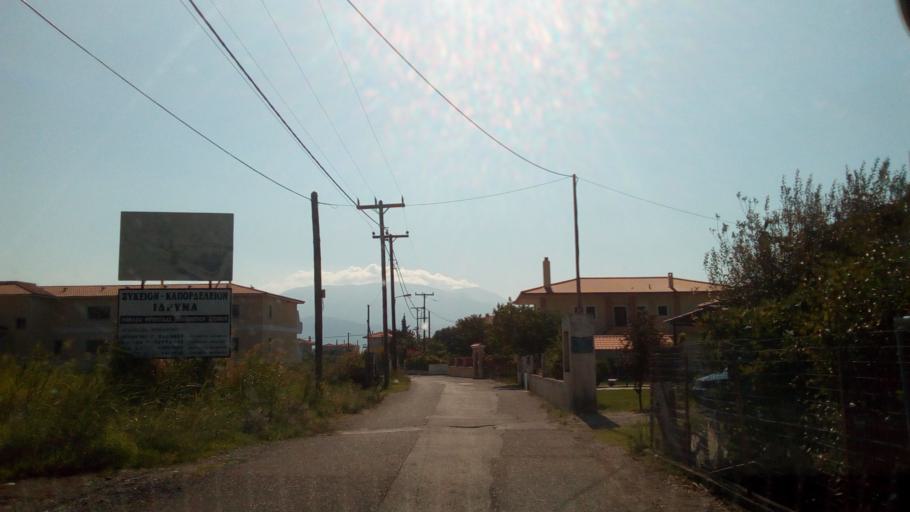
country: GR
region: West Greece
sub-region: Nomos Aitolias kai Akarnanias
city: Nafpaktos
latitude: 38.3777
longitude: 21.7938
